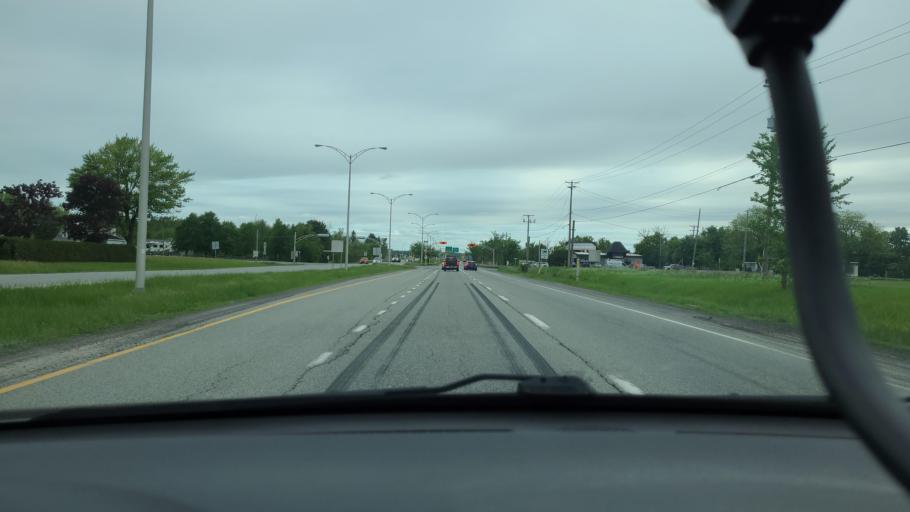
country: CA
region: Quebec
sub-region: Lanaudiere
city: Sainte-Julienne
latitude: 45.8957
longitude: -73.6598
